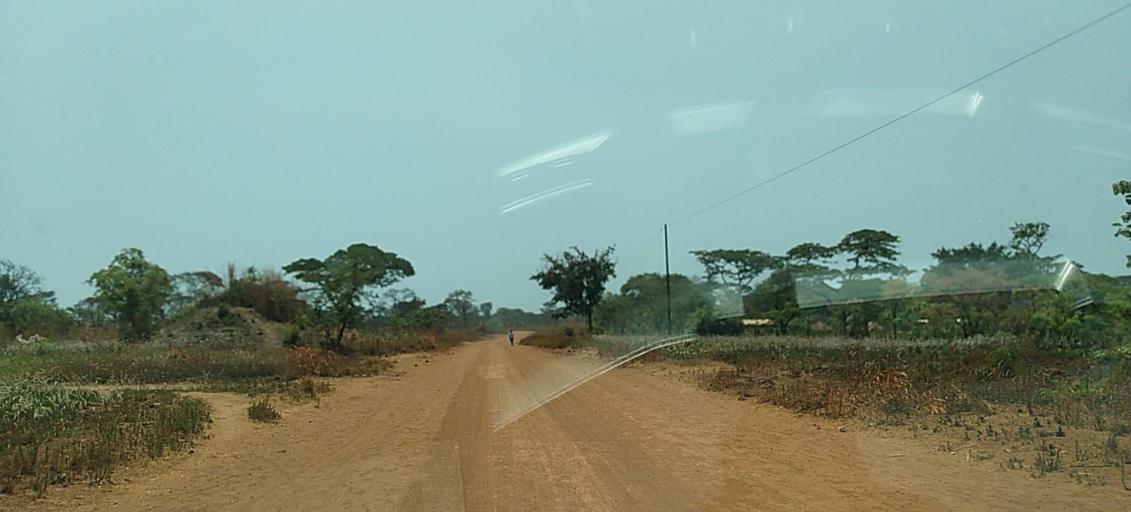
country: CD
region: Katanga
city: Kipushi
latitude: -11.9357
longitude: 26.9635
